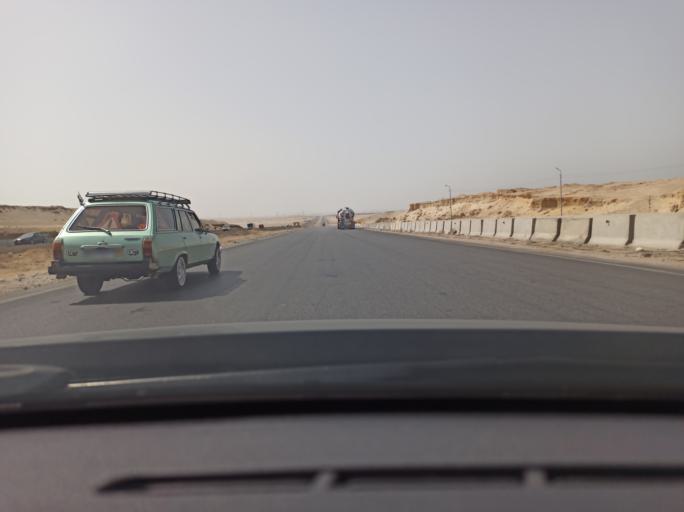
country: EG
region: Muhafazat al Fayyum
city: Al Wasitah
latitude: 29.3736
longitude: 31.3095
